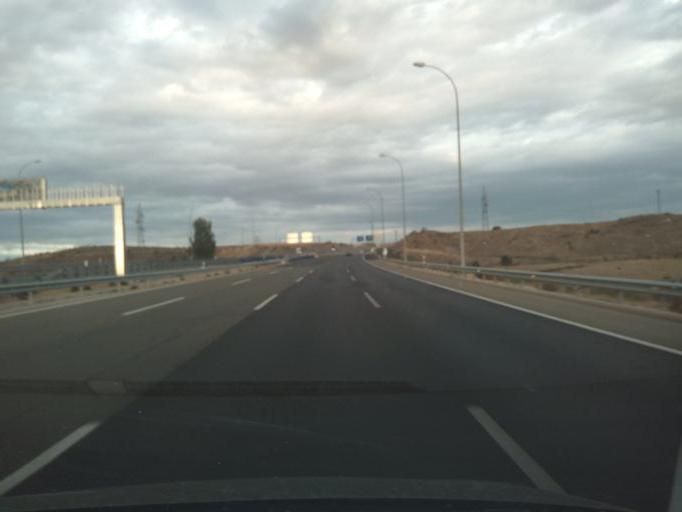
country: ES
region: Madrid
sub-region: Provincia de Madrid
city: Paracuellos de Jarama
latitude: 40.5440
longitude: -3.5519
